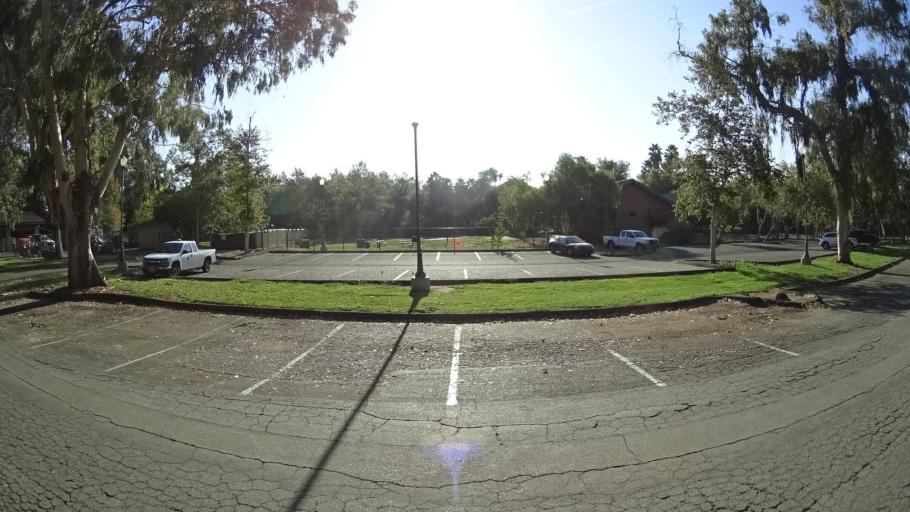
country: US
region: California
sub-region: San Diego County
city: Escondido
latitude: 33.0811
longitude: -117.0607
